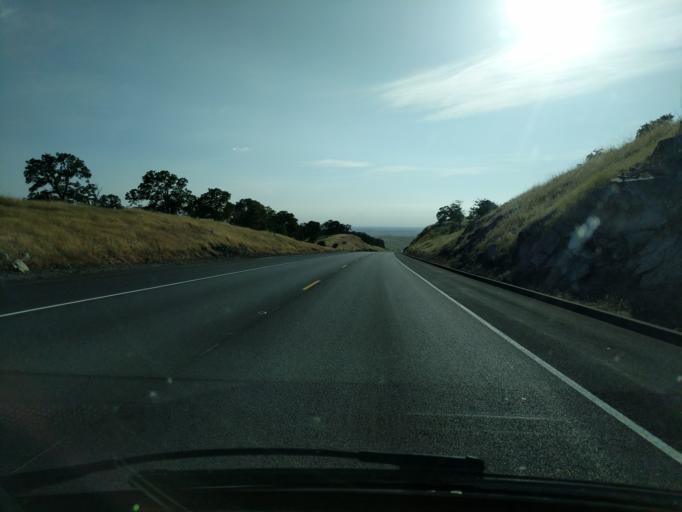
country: US
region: California
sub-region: Calaveras County
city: Copperopolis
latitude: 37.9414
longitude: -120.7412
